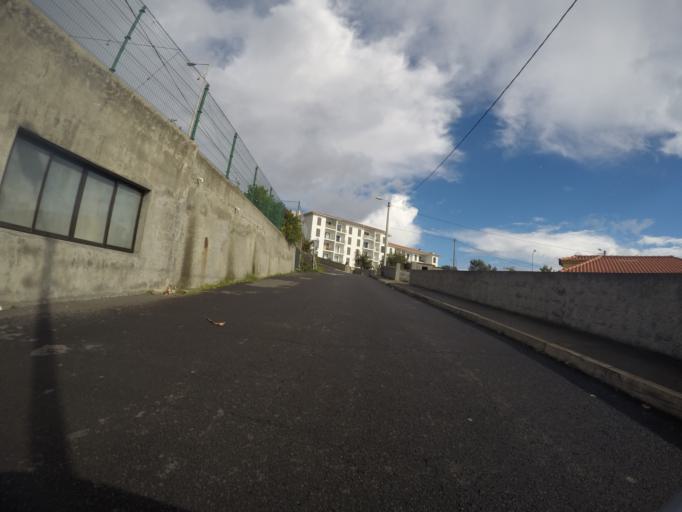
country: PT
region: Madeira
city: Canico
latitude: 32.6478
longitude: -16.8541
